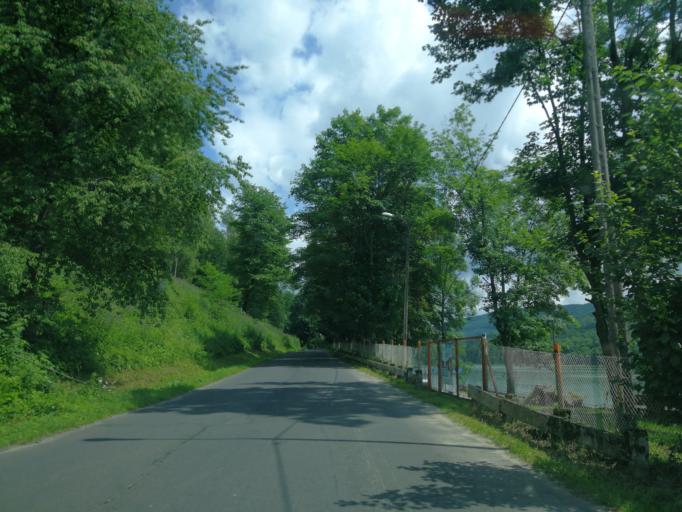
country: PL
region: Subcarpathian Voivodeship
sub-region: Powiat leski
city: Uherce Mineralne
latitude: 49.4305
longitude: 22.4130
